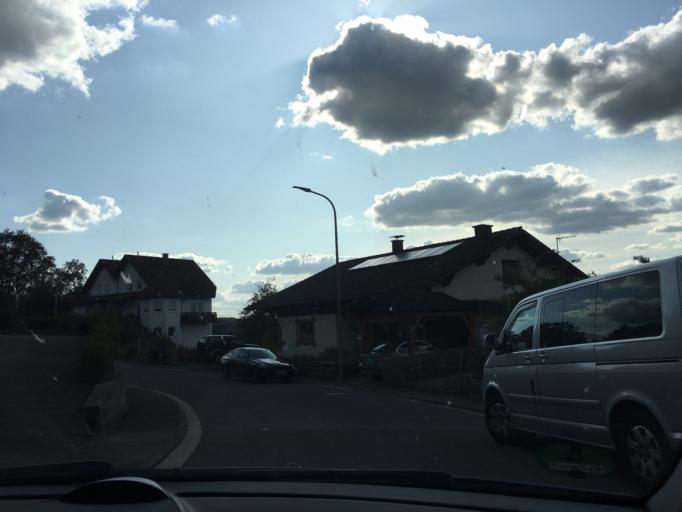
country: DE
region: Rheinland-Pfalz
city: Schopp
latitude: 49.3470
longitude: 7.6854
